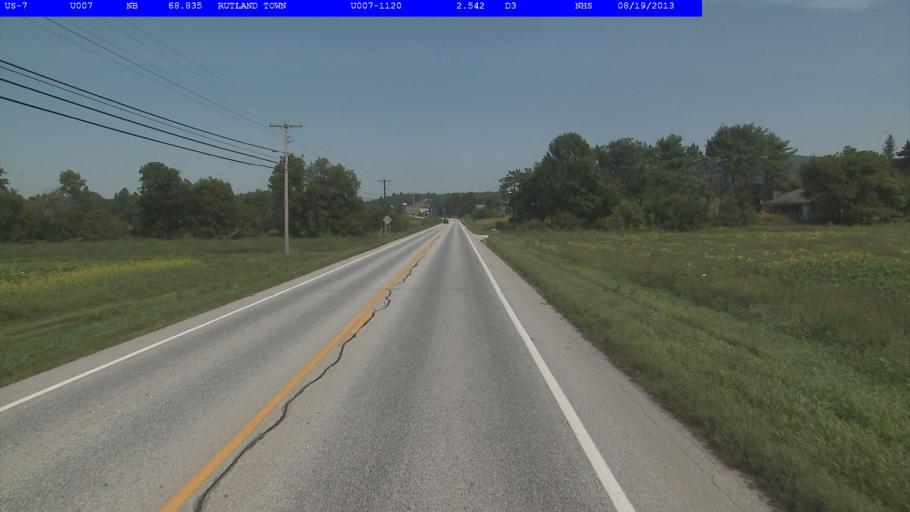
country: US
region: Vermont
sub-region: Rutland County
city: Rutland
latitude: 43.6474
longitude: -72.9855
